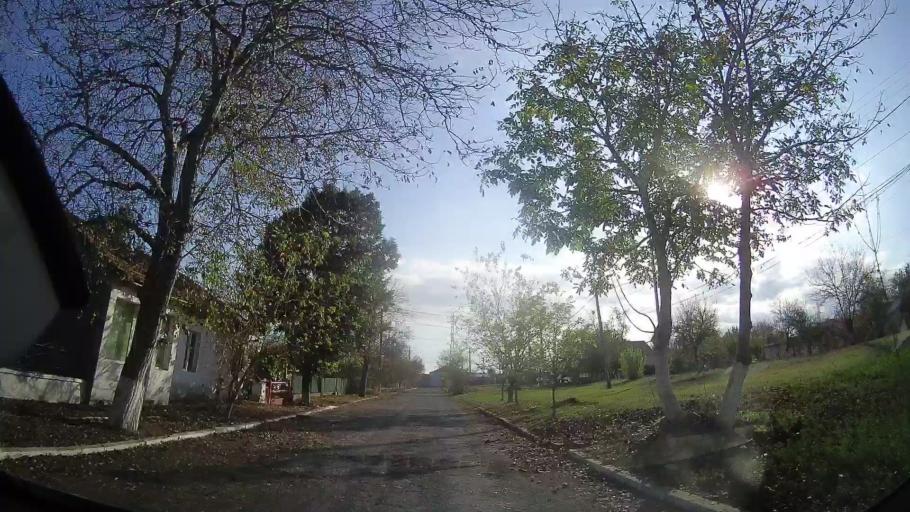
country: RO
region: Constanta
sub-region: Comuna Limanu
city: Limanu
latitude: 43.7957
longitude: 28.5302
